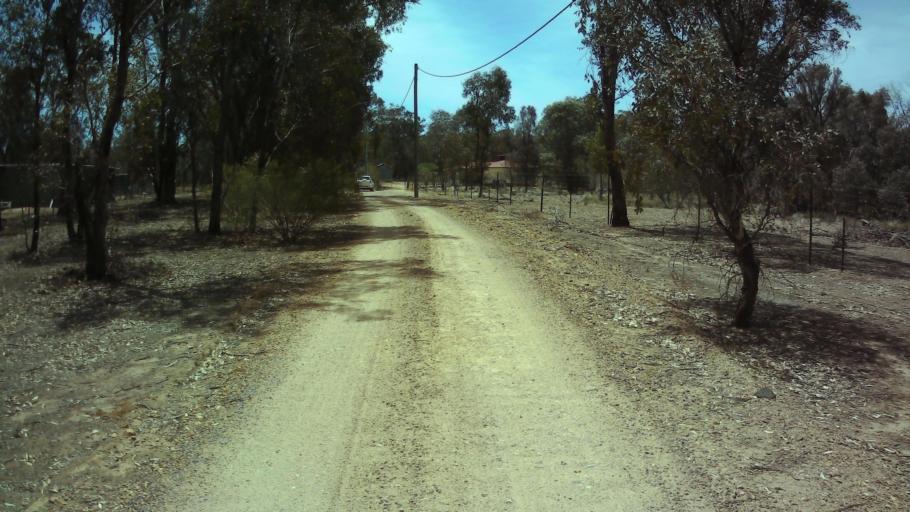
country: AU
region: New South Wales
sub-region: Weddin
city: Grenfell
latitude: -33.8870
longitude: 148.1696
